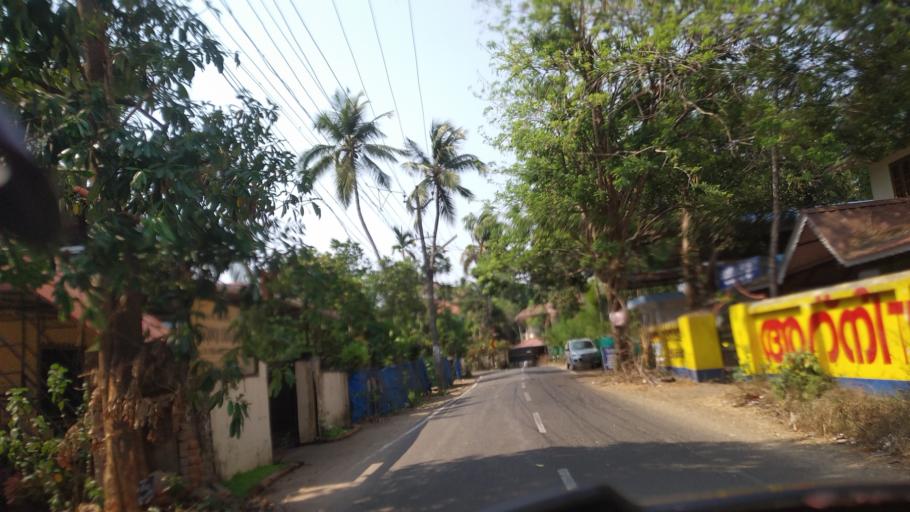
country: IN
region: Kerala
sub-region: Thrissur District
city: Thanniyam
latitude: 10.4097
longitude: 76.0943
